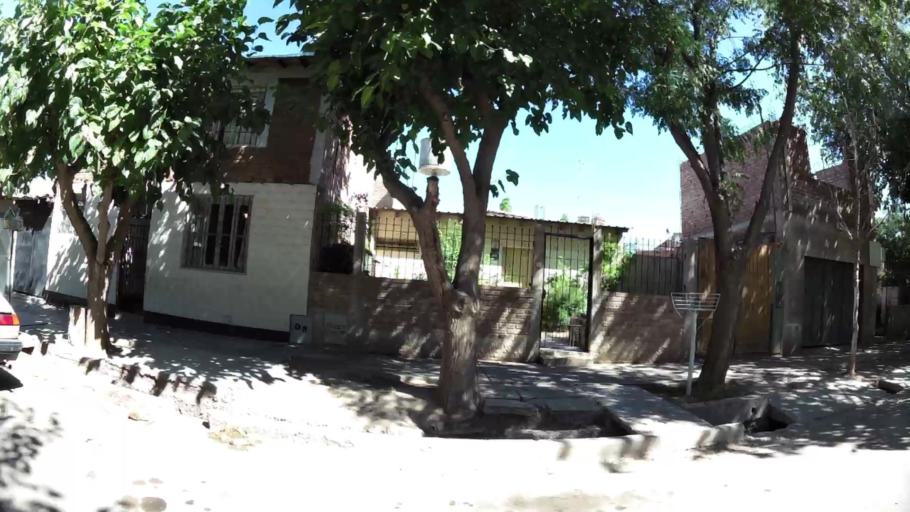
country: AR
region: Mendoza
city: Las Heras
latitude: -32.8276
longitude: -68.8376
